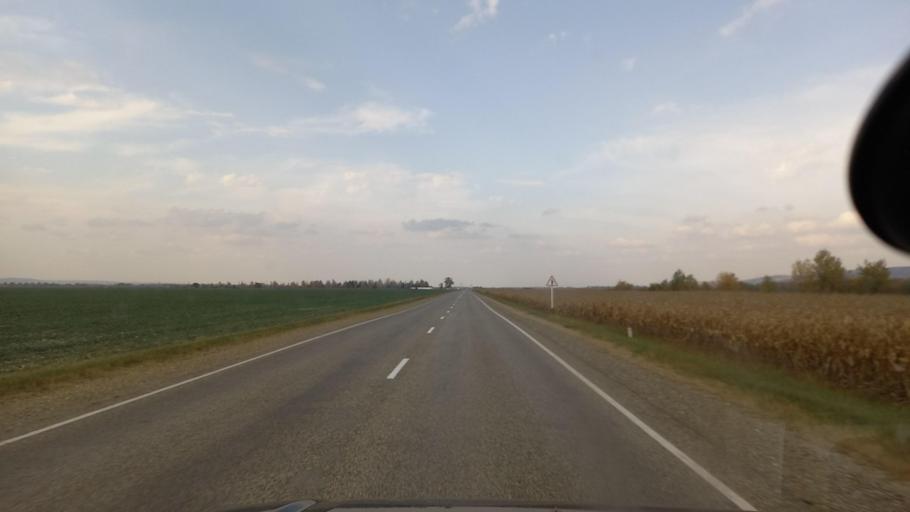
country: RU
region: Krasnodarskiy
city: Perepravnaya
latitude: 44.3399
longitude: 40.8444
